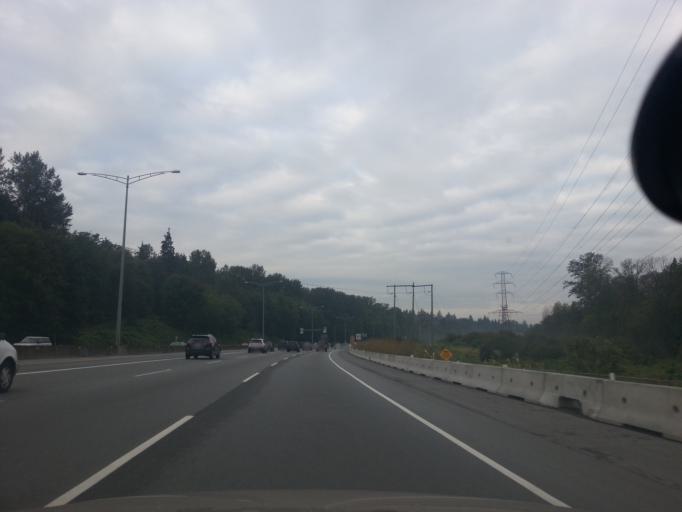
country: CA
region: British Columbia
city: New Westminster
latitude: 49.2383
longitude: -122.9229
